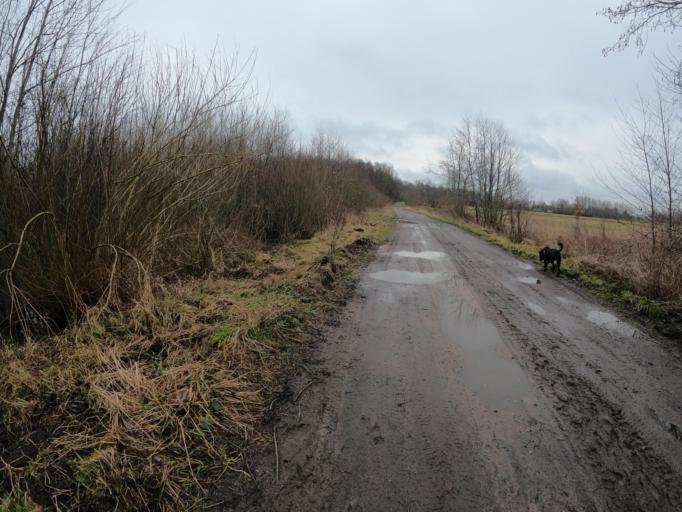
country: PL
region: West Pomeranian Voivodeship
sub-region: Powiat slawienski
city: Darlowo
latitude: 54.4004
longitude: 16.4486
